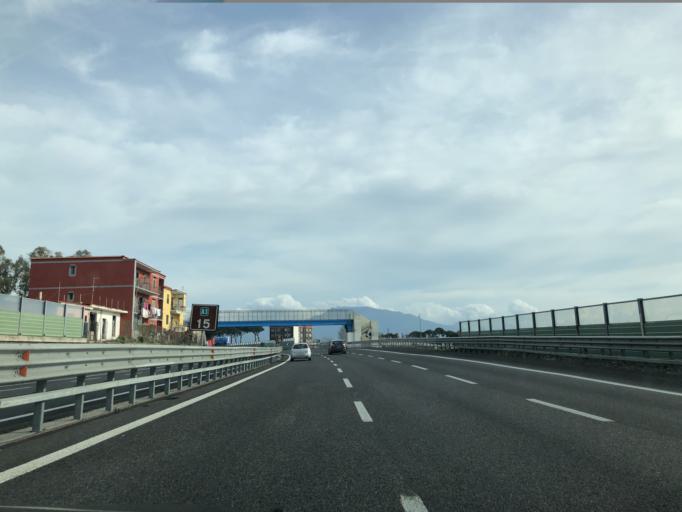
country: IT
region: Campania
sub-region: Provincia di Napoli
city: Torre del Greco
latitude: 40.7815
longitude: 14.3905
